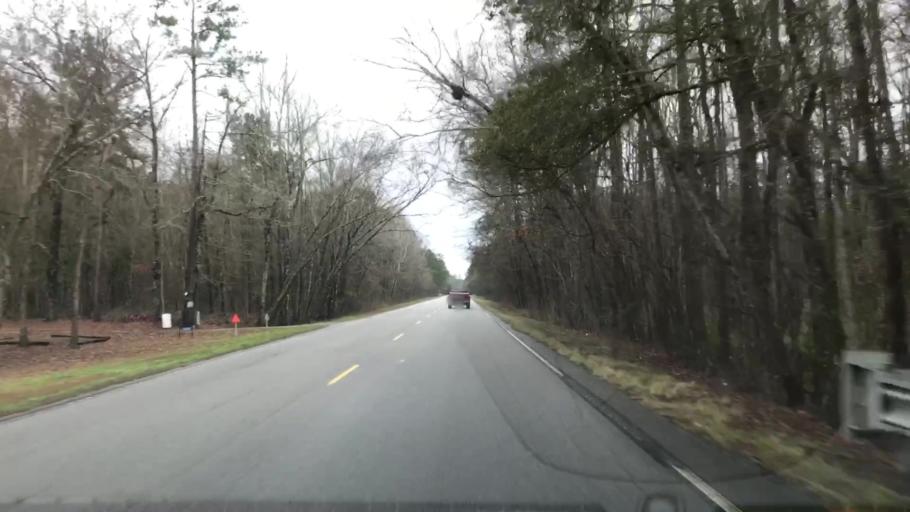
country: US
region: South Carolina
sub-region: Williamsburg County
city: Andrews
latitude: 33.5288
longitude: -79.4883
